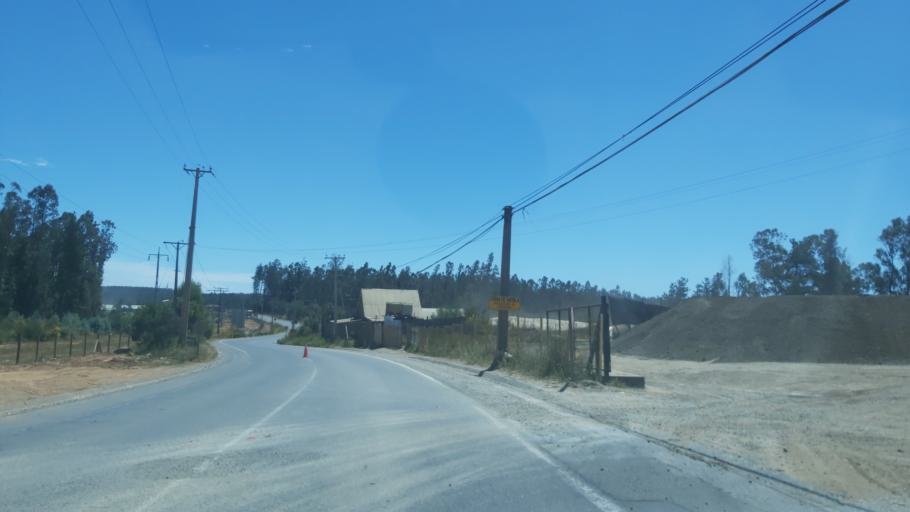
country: CL
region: Maule
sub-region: Provincia de Talca
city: Constitucion
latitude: -35.3675
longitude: -72.4039
